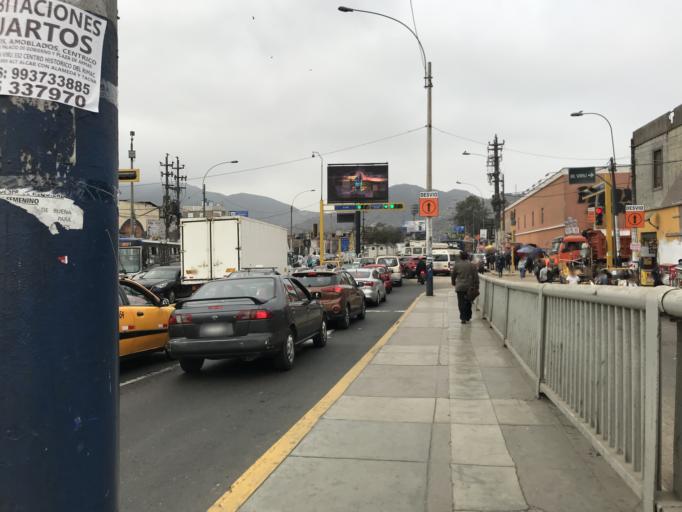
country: PE
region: Lima
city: Lima
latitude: -12.0401
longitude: -77.0331
